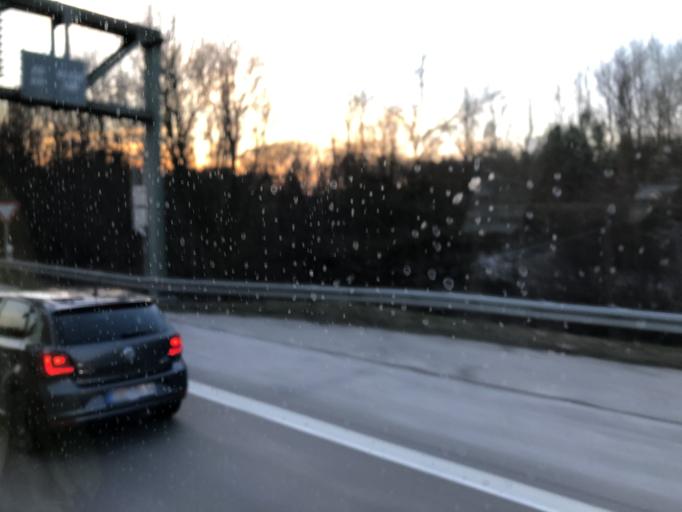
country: DE
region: Bavaria
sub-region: Upper Bavaria
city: Hallbergmoos
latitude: 48.3496
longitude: 11.7248
